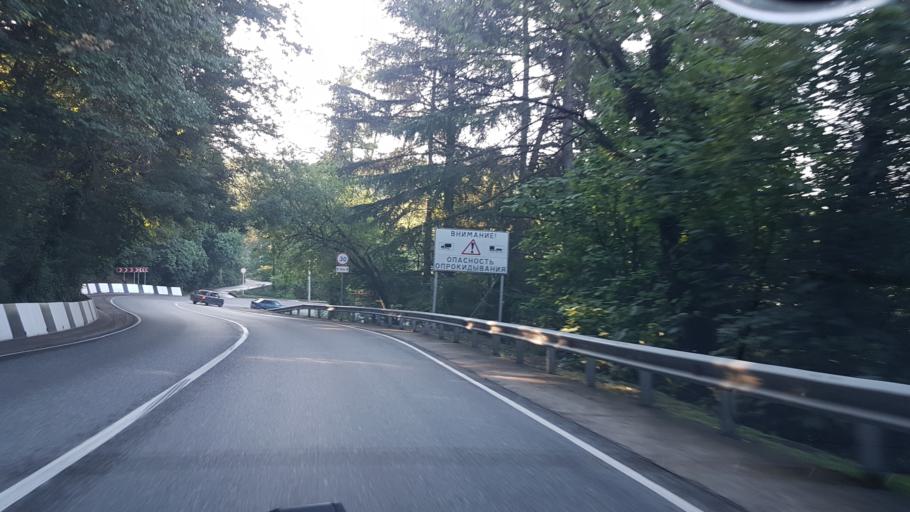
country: RU
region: Krasnodarskiy
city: Dagomys
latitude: 43.6678
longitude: 39.6248
